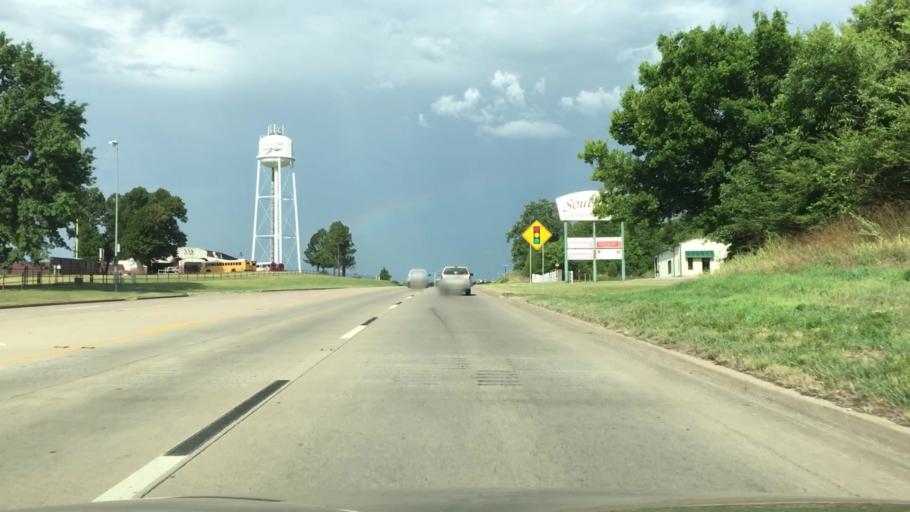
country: US
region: Oklahoma
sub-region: Cherokee County
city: Park Hill
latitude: 35.8506
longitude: -94.9990
